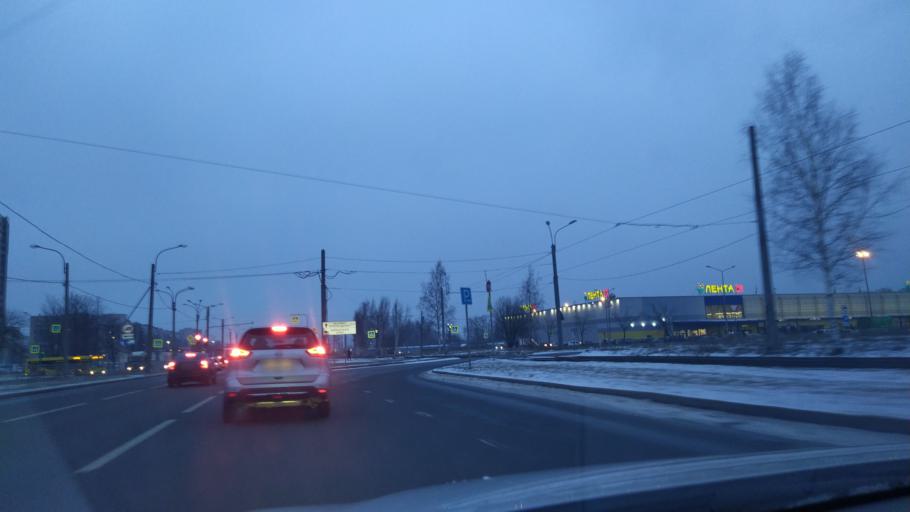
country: RU
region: Leningrad
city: Murino
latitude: 60.0297
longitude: 30.4322
